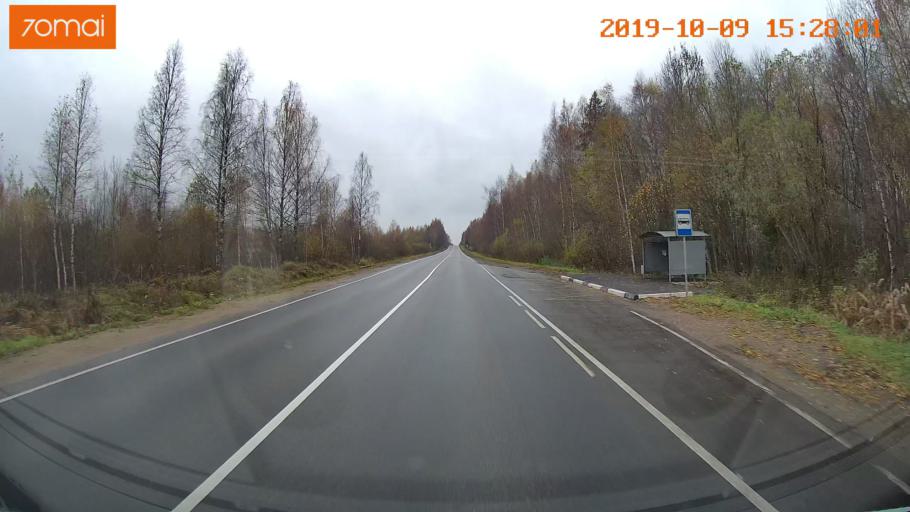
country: RU
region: Kostroma
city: Susanino
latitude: 58.0079
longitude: 41.3670
